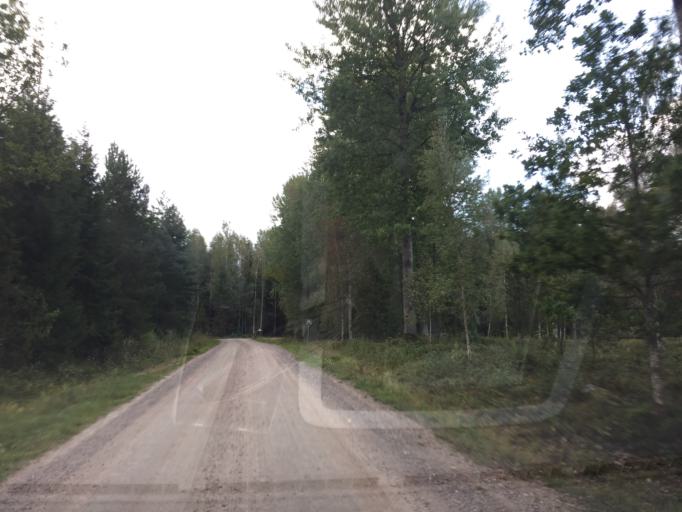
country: SE
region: Soedermanland
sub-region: Vingakers Kommun
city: Vingaker
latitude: 58.9961
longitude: 15.7395
